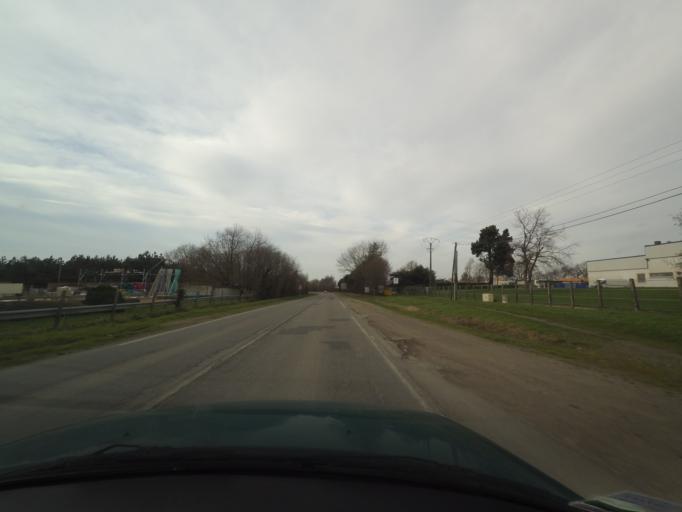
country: FR
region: Pays de la Loire
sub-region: Departement de la Loire-Atlantique
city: Saint-Pere-en-Retz
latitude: 47.1991
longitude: -2.0335
